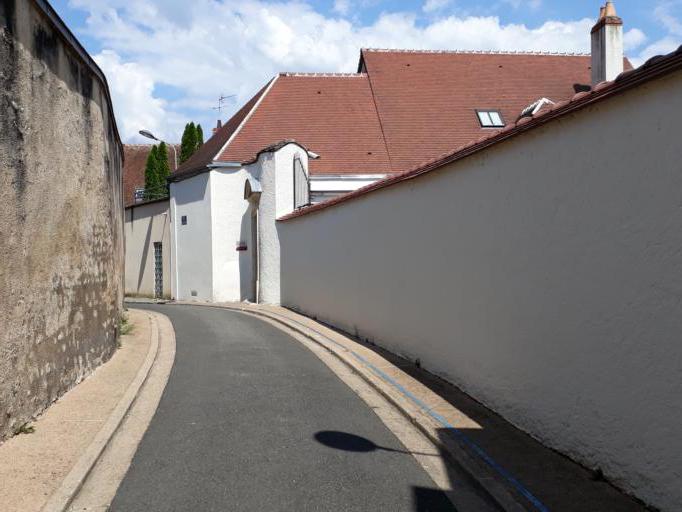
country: FR
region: Bourgogne
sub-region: Departement de la Nievre
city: Nevers
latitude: 46.9862
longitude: 3.1573
